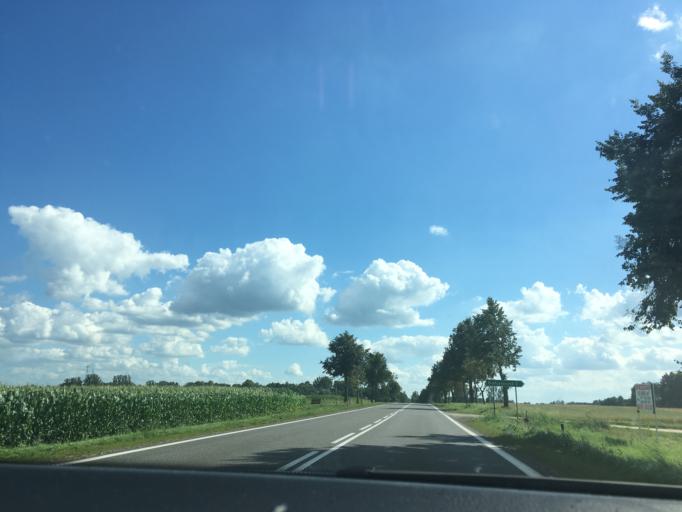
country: PL
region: Podlasie
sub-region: Powiat sokolski
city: Janow
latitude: 53.4012
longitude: 23.1159
